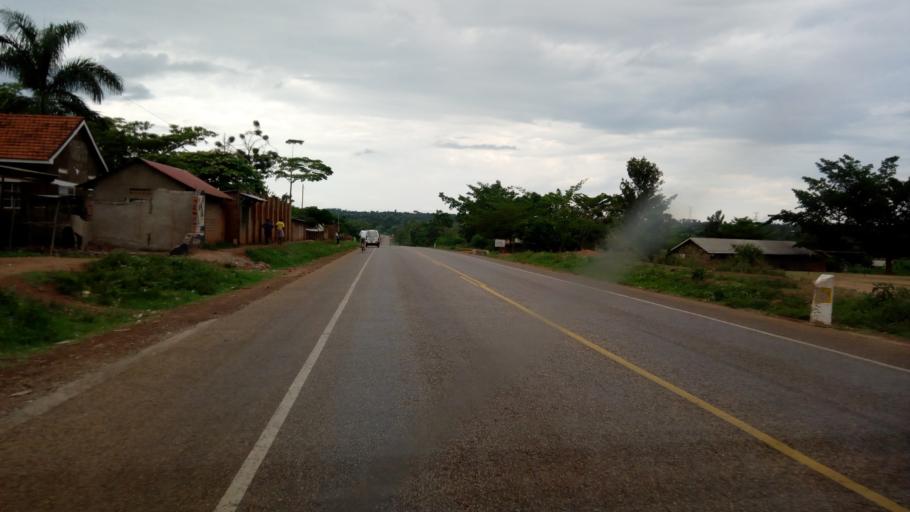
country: UG
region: Eastern Region
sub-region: Mbale District
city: Mbale
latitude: 0.9923
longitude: 34.1669
